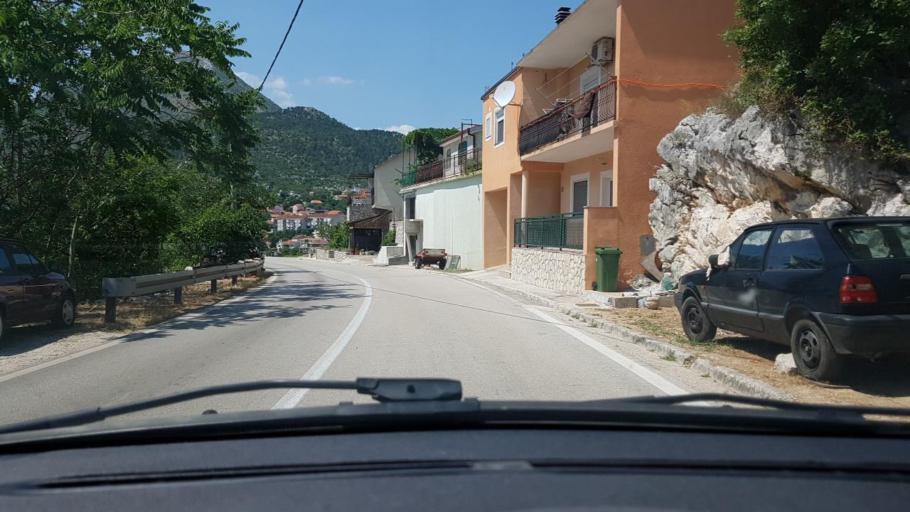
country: HR
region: Splitsko-Dalmatinska
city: Vrgorac
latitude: 43.2005
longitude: 17.3766
